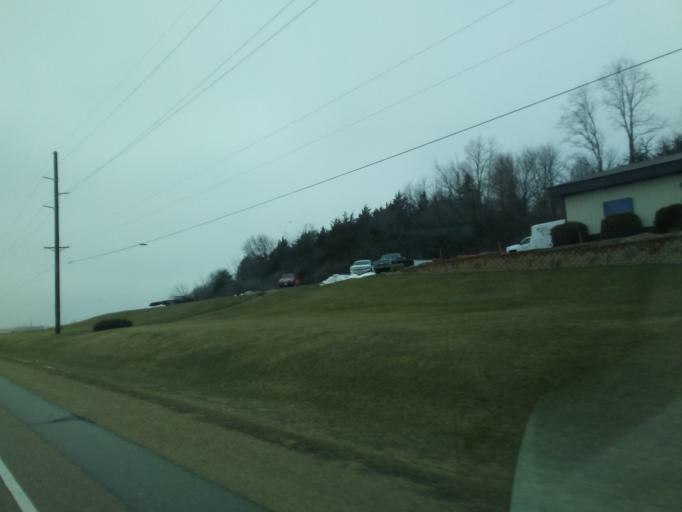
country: US
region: Wisconsin
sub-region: Dane County
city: Black Earth
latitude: 43.1490
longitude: -89.7611
